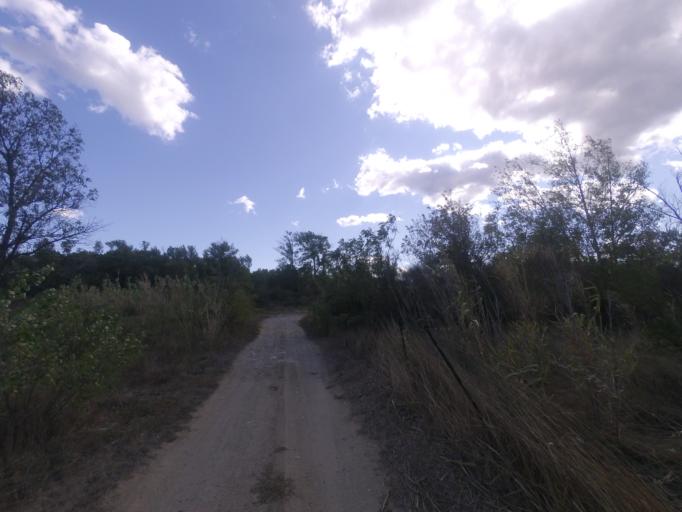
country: FR
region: Languedoc-Roussillon
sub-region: Departement des Pyrenees-Orientales
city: Corneilla-la-Riviere
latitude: 42.6936
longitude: 2.7166
